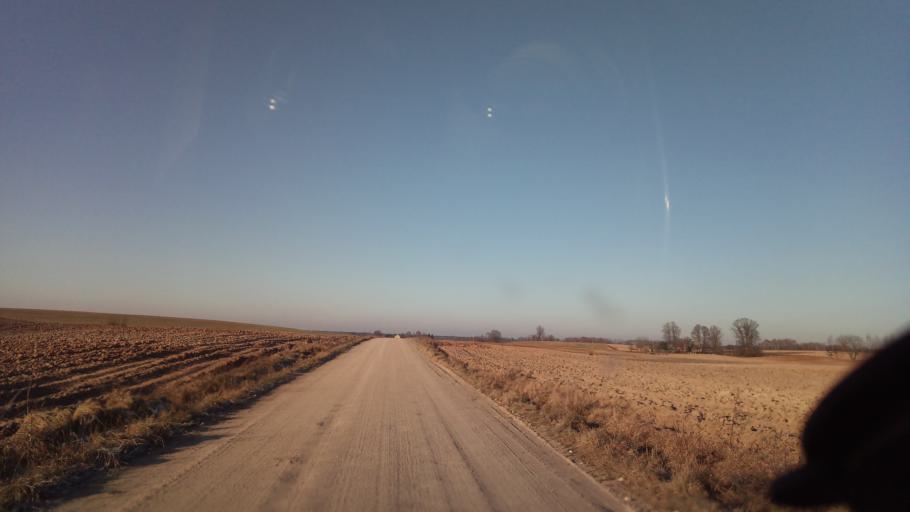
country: LT
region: Alytaus apskritis
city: Druskininkai
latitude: 54.0906
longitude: 24.0011
